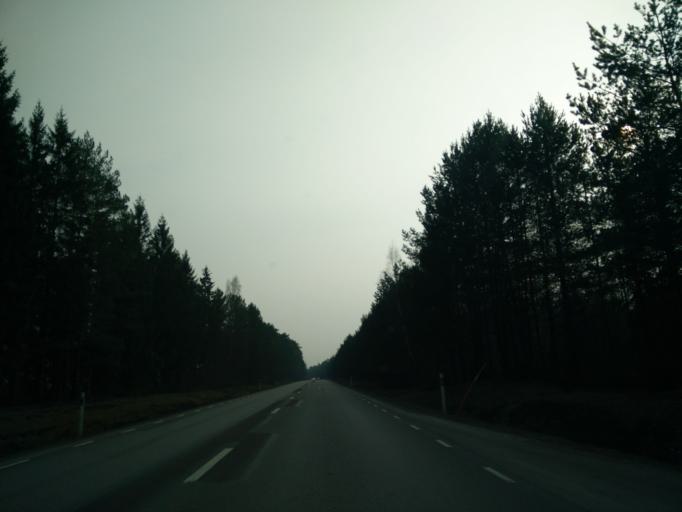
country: SE
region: Vaermland
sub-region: Forshaga Kommun
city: Forshaga
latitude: 59.4891
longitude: 13.4214
